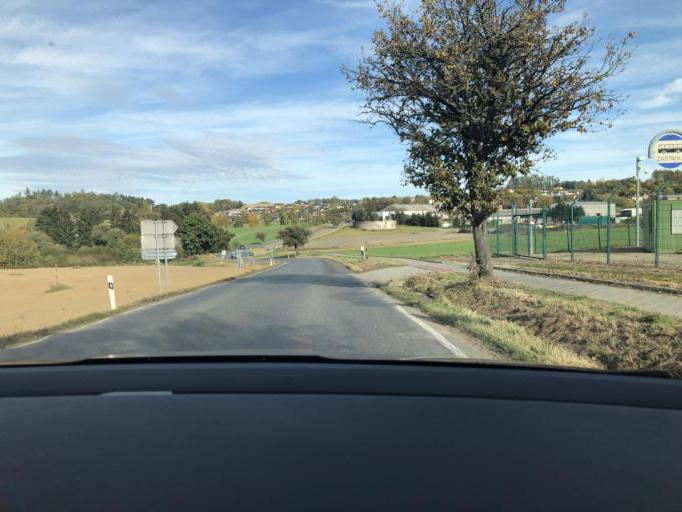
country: CZ
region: Central Bohemia
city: Postupice
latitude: 49.7629
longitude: 14.7504
